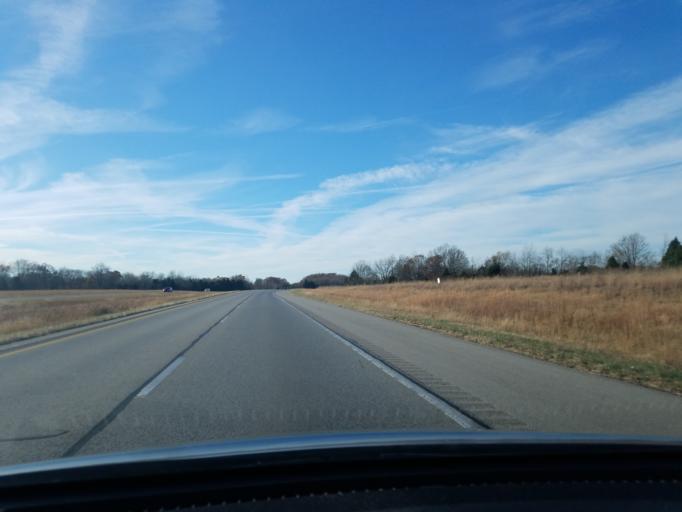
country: US
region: Indiana
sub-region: Harrison County
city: Corydon
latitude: 38.2504
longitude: -86.2710
